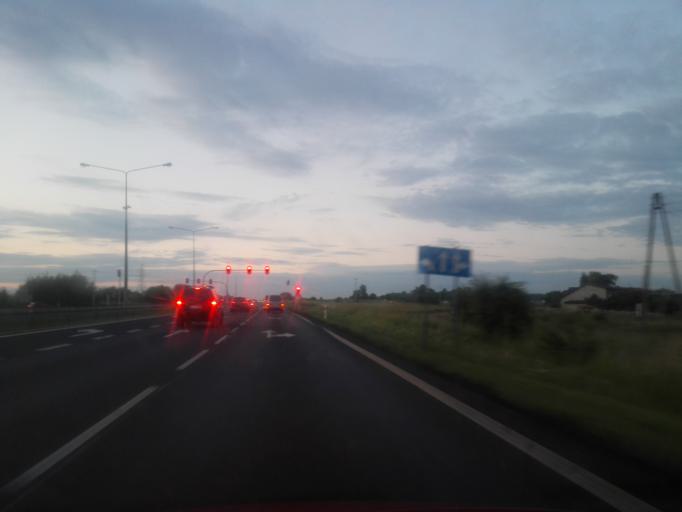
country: PL
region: Lodz Voivodeship
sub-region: Powiat piotrkowski
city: Wola Krzysztoporska
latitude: 51.3205
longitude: 19.5785
